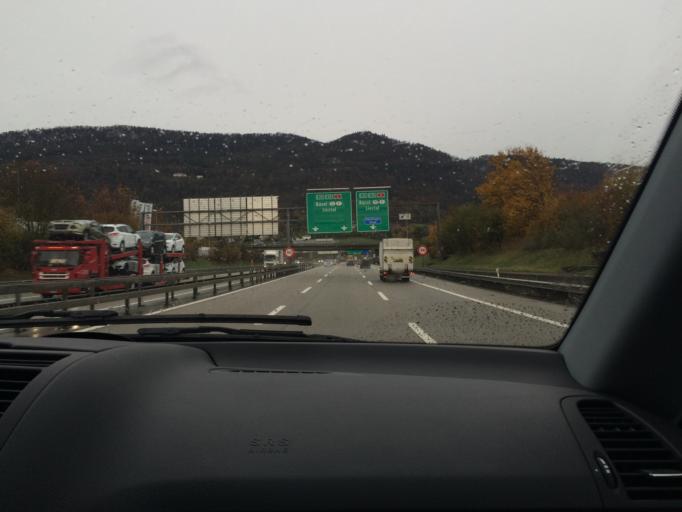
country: CH
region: Solothurn
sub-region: Bezirk Gaeu
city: Egerkingen
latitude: 47.3174
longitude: 7.8059
